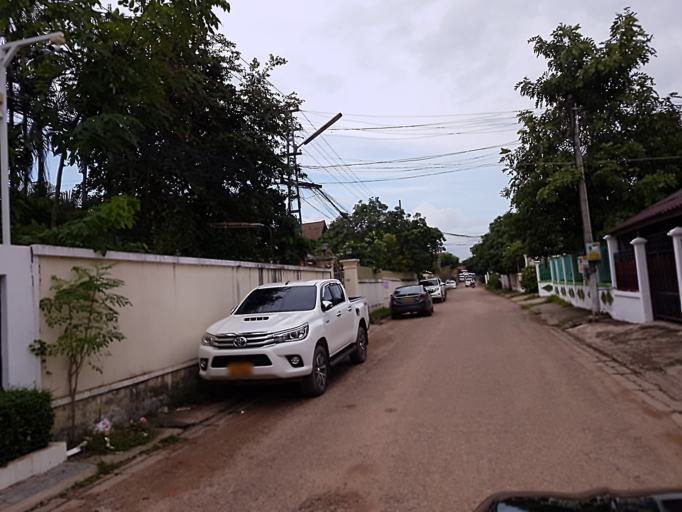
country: LA
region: Vientiane
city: Vientiane
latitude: 17.9513
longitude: 102.6250
